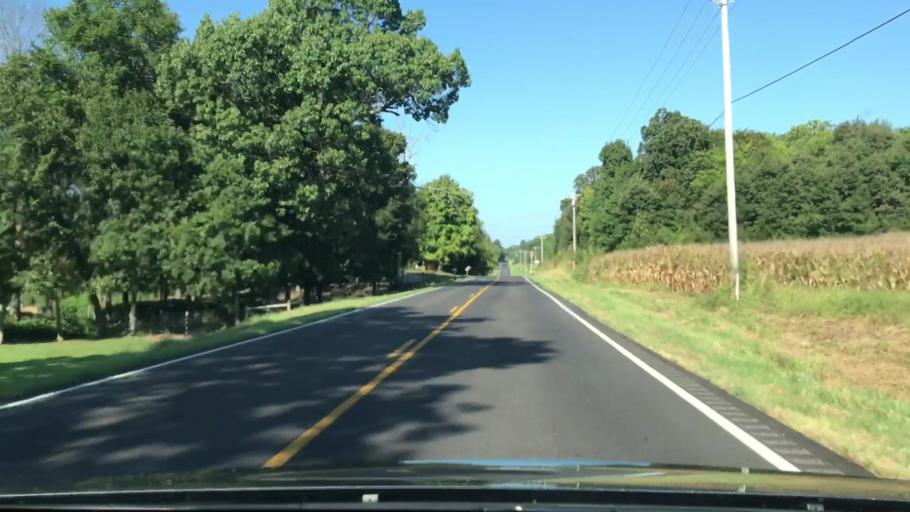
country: US
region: Kentucky
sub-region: Marshall County
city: Benton
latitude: 36.7647
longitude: -88.3221
